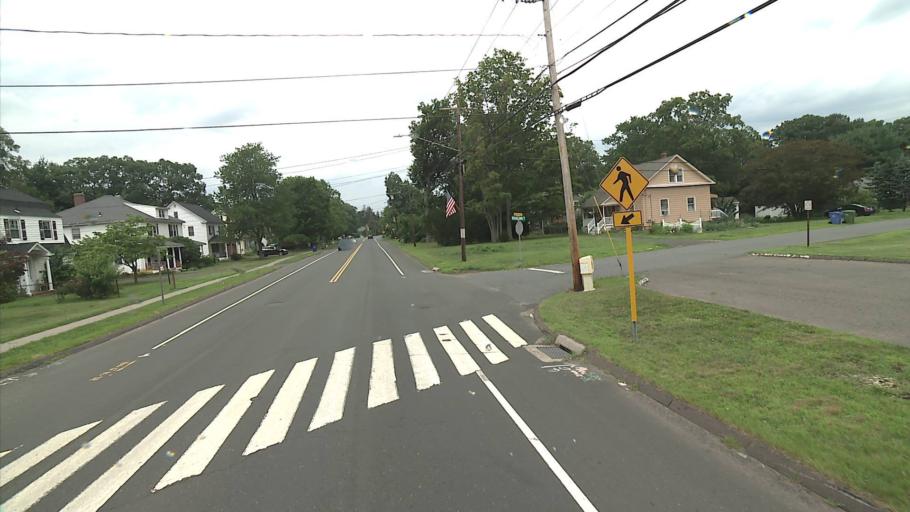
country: US
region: Connecticut
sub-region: Middlesex County
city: Cromwell
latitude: 41.6213
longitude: -72.6537
